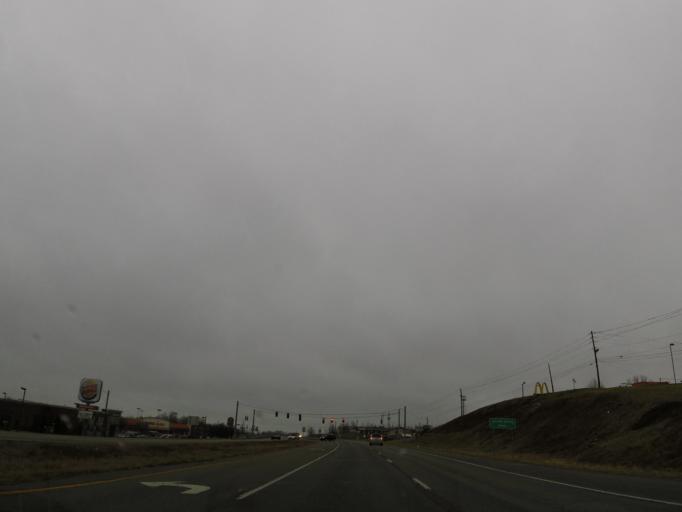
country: US
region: Kentucky
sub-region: Boyle County
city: Danville
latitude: 37.6176
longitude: -84.7732
